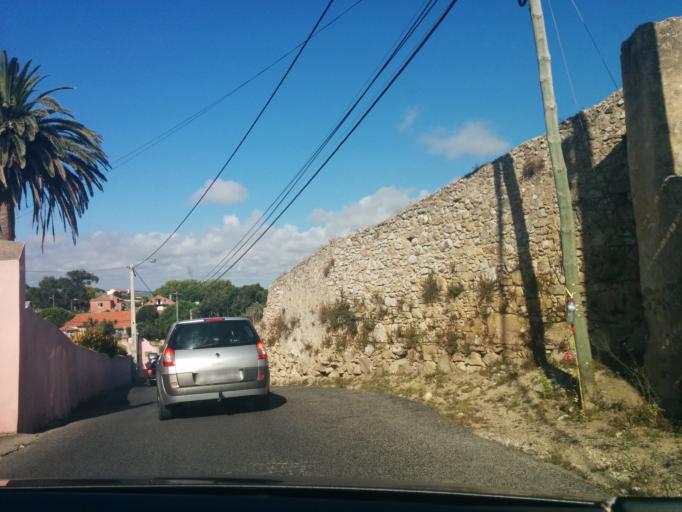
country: PT
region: Lisbon
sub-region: Sintra
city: Colares
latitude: 38.7976
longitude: -9.4685
